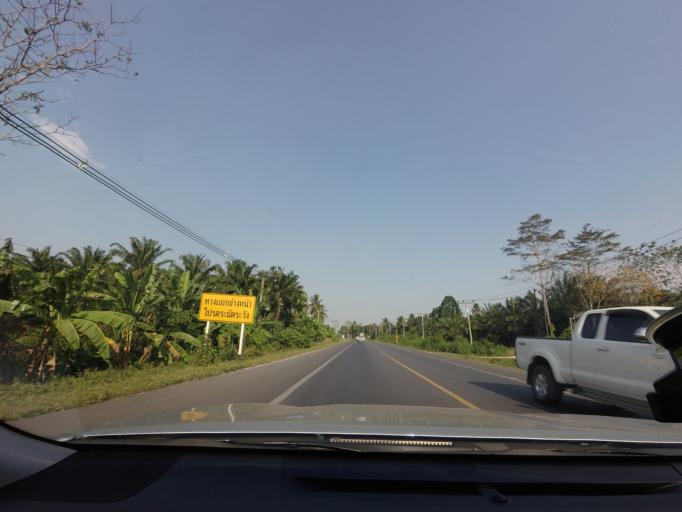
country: TH
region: Surat Thani
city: Phrasaeng
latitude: 8.5714
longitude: 99.2023
